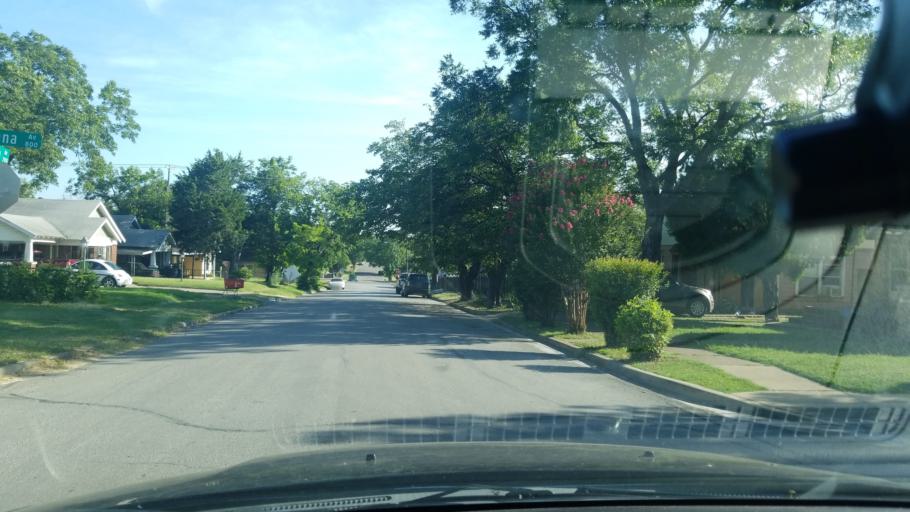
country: US
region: Texas
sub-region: Dallas County
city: Dallas
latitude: 32.7214
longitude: -96.8121
